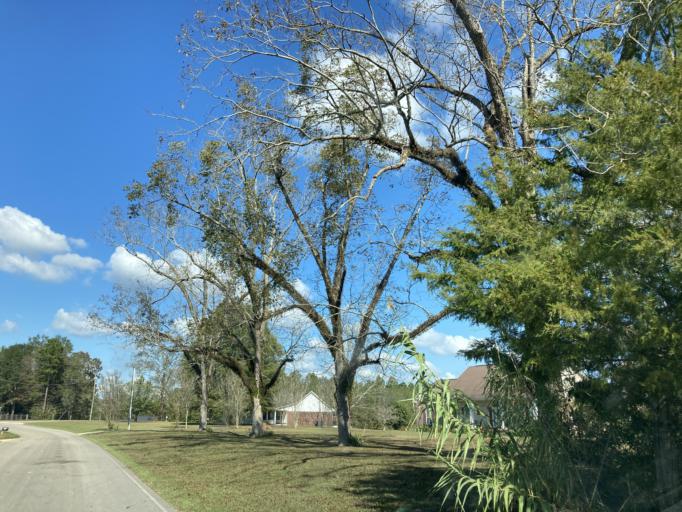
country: US
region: Mississippi
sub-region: Lamar County
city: Sumrall
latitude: 31.3343
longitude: -89.5399
